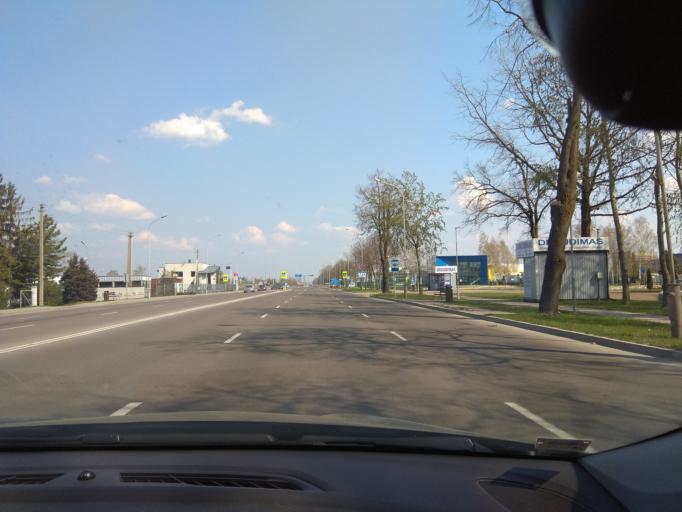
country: LT
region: Marijampoles apskritis
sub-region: Marijampole Municipality
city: Marijampole
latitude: 54.5796
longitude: 23.3747
